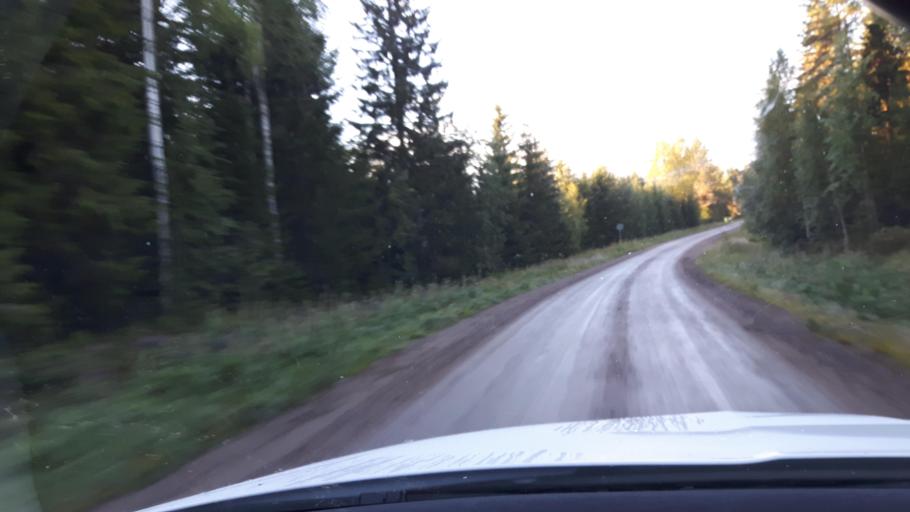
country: SE
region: Vaesternorrland
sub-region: Ange Kommun
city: Ange
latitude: 62.1442
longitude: 15.6610
